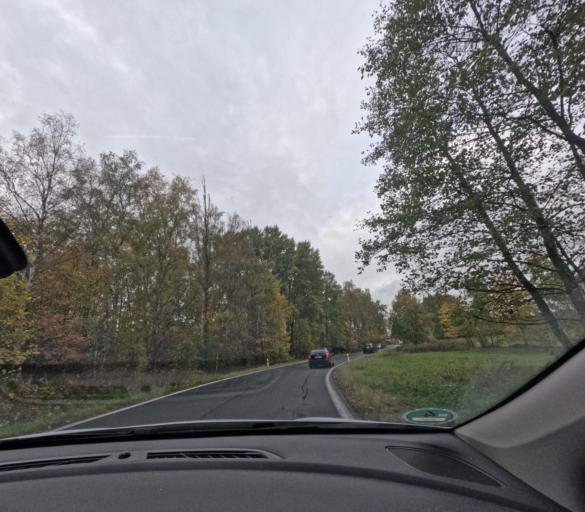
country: CZ
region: Karlovarsky
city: Dalovice
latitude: 50.2089
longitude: 12.9078
